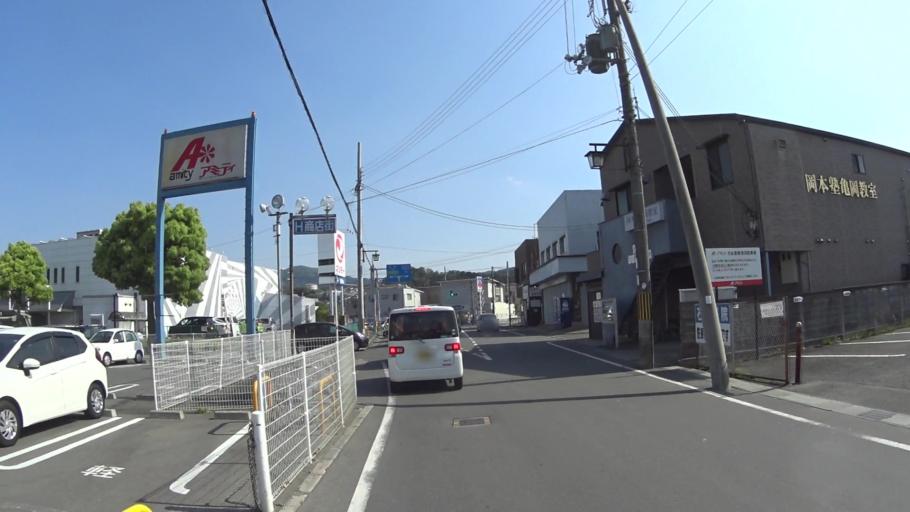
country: JP
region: Kyoto
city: Kameoka
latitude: 35.0065
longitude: 135.5838
